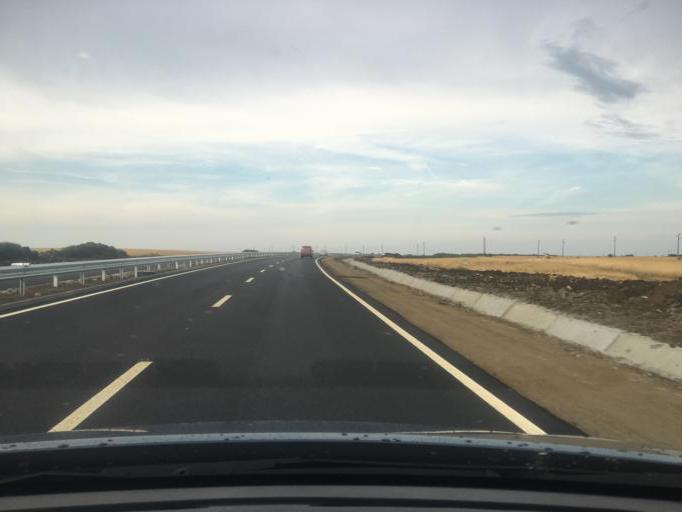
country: BG
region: Burgas
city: Aheloy
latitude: 42.6563
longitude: 27.6525
